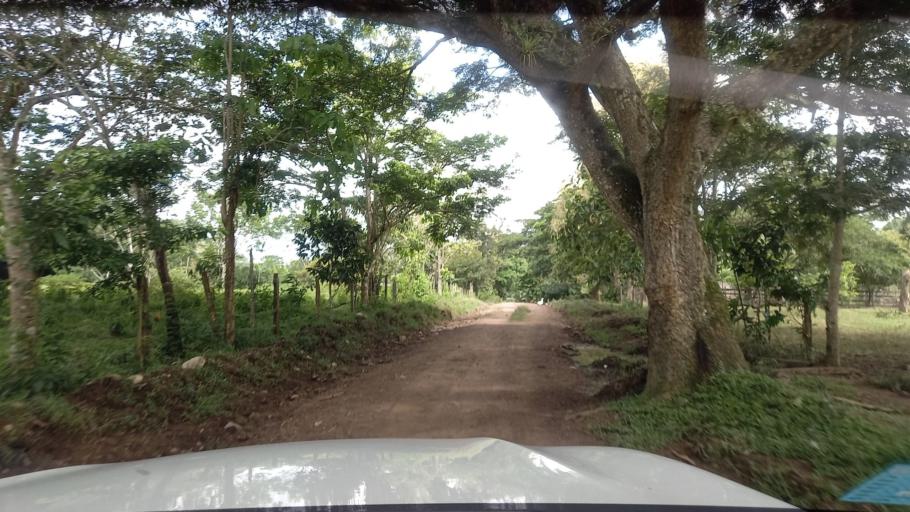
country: NI
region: Jinotega
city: San Jose de Bocay
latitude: 13.4139
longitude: -85.7033
